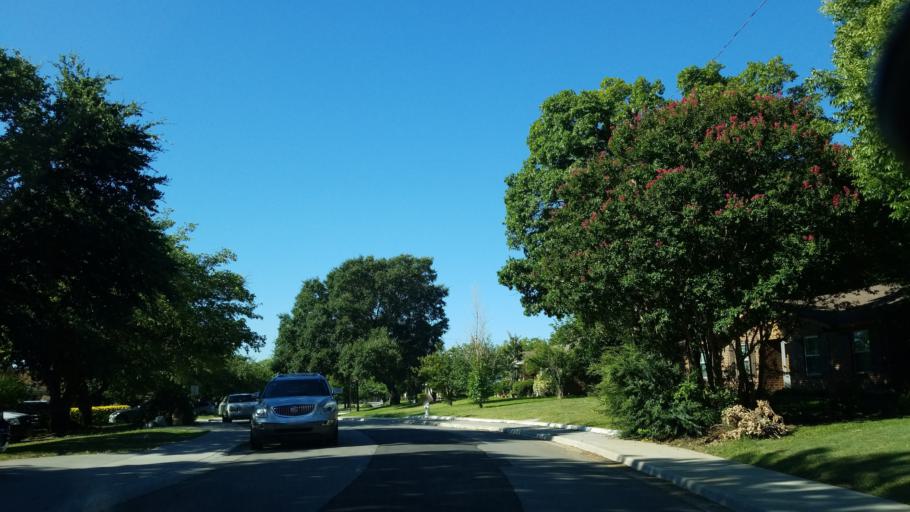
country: US
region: Texas
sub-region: Dallas County
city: Carrollton
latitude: 32.9448
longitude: -96.8853
